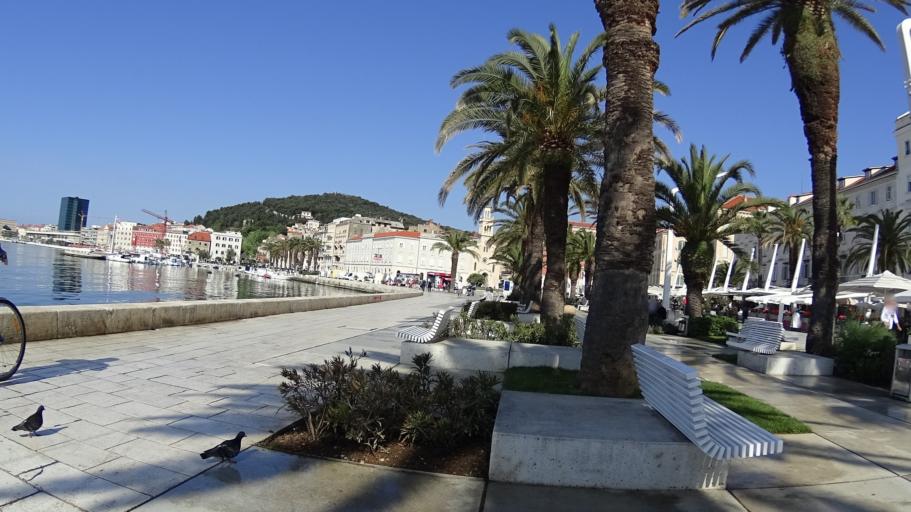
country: HR
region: Splitsko-Dalmatinska
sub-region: Grad Split
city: Split
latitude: 43.5079
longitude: 16.4375
